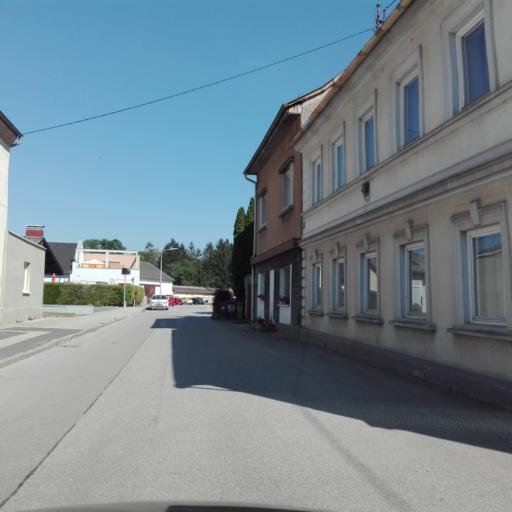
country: AT
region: Upper Austria
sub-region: Politischer Bezirk Linz-Land
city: Ansfelden
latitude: 48.2307
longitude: 14.2681
